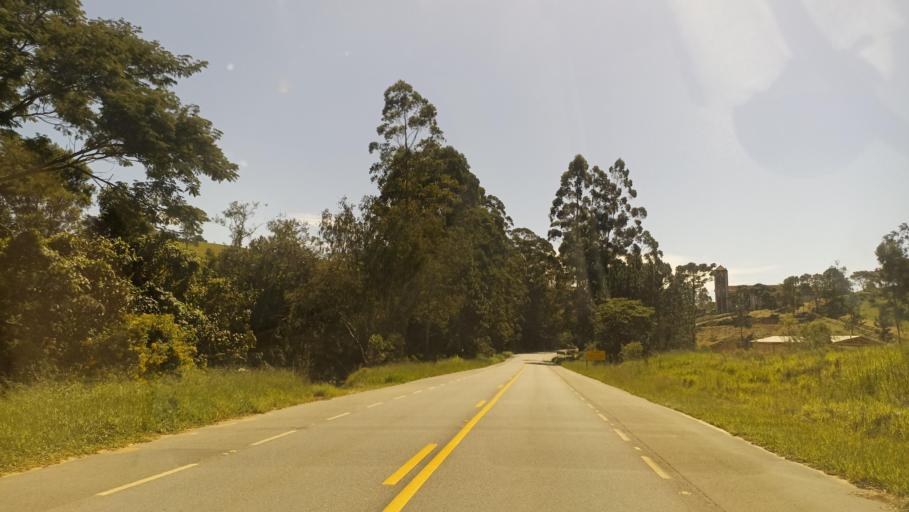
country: BR
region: Sao Paulo
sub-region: Guaratingueta
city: Guaratingueta
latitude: -22.9299
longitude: -45.0776
